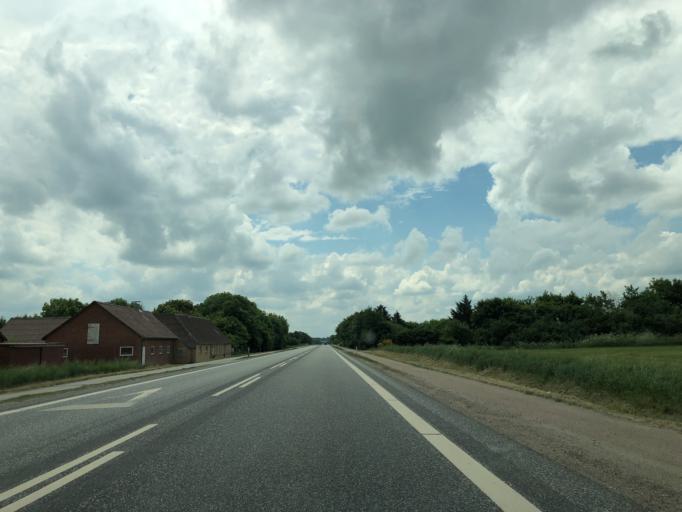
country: DK
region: Central Jutland
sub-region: Struer Kommune
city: Struer
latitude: 56.4713
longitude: 8.5865
